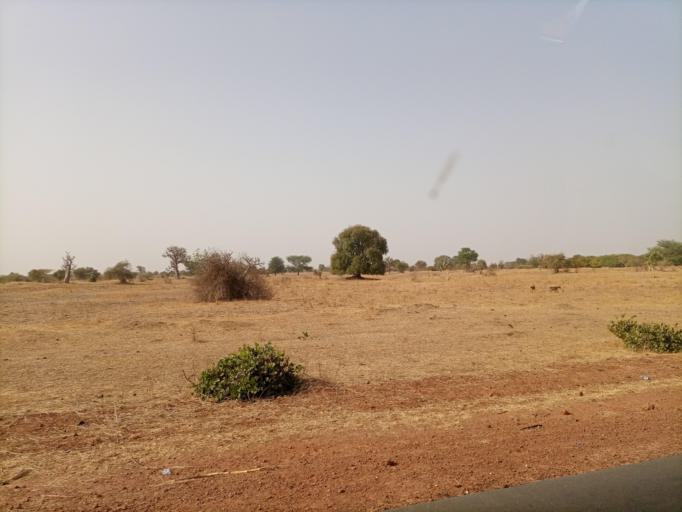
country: SN
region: Fatick
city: Foundiougne
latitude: 14.1290
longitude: -16.4081
